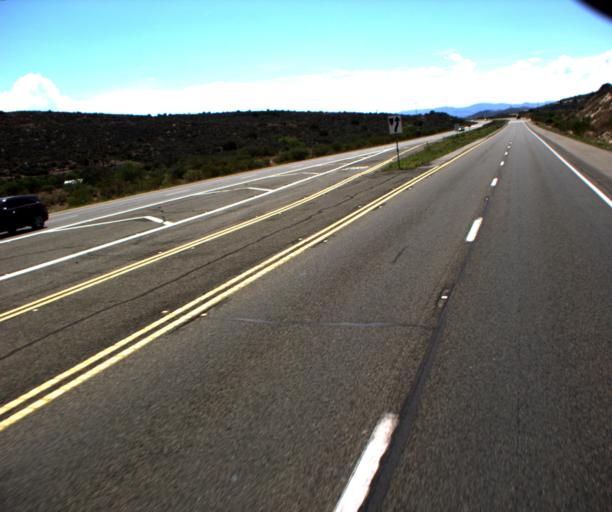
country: US
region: Arizona
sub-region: Yavapai County
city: Mayer
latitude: 34.3789
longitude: -112.1948
